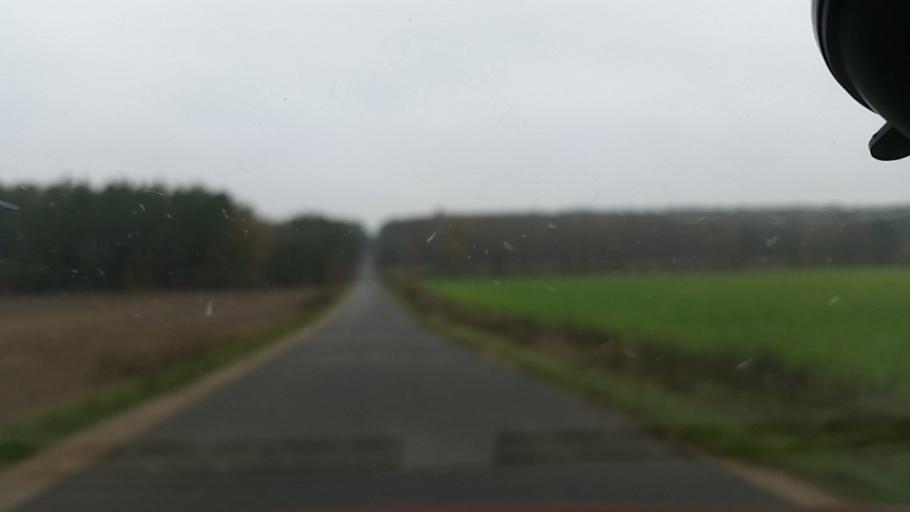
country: DE
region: Lower Saxony
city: Stadensen
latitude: 52.8374
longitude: 10.5540
